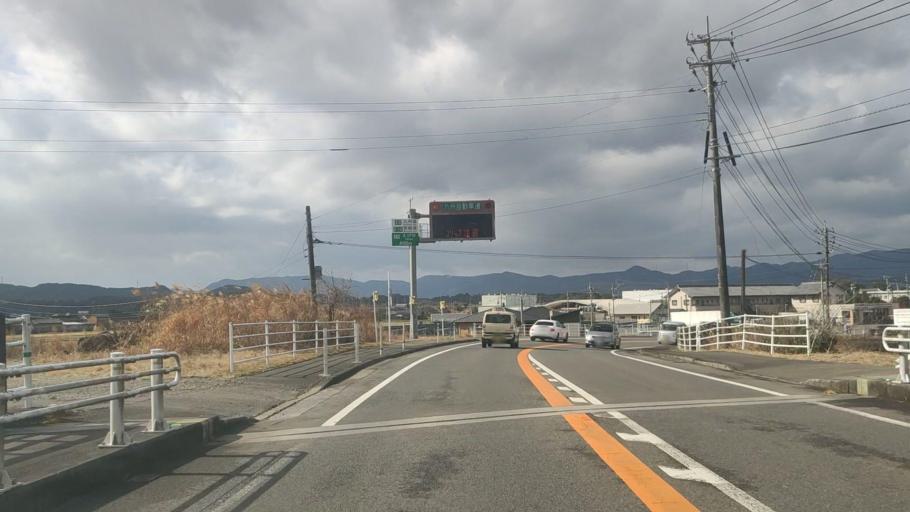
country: JP
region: Kumamoto
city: Hitoyoshi
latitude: 32.0500
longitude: 130.8083
